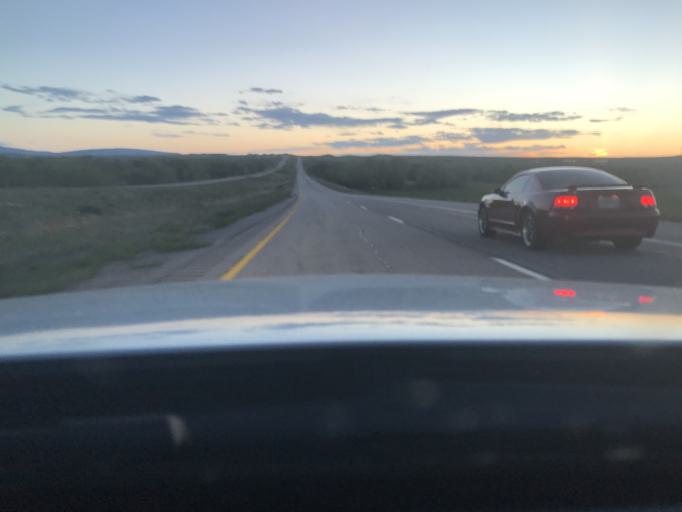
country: US
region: Wyoming
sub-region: Converse County
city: Glenrock
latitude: 42.8374
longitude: -105.8622
